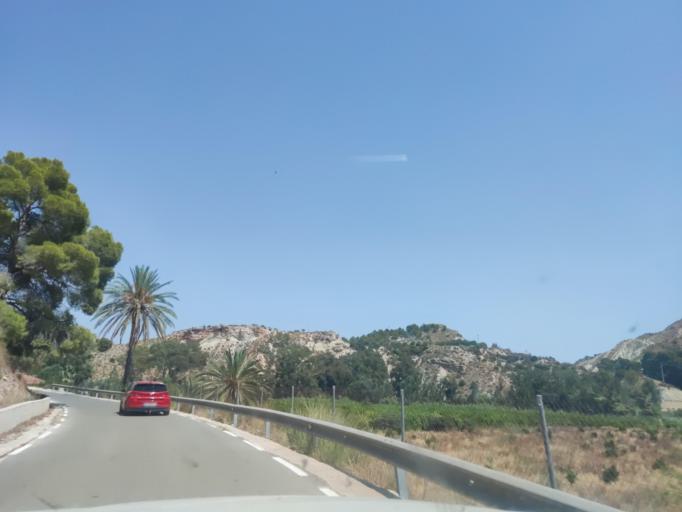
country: ES
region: Murcia
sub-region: Murcia
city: Archena
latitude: 38.1288
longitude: -1.3101
